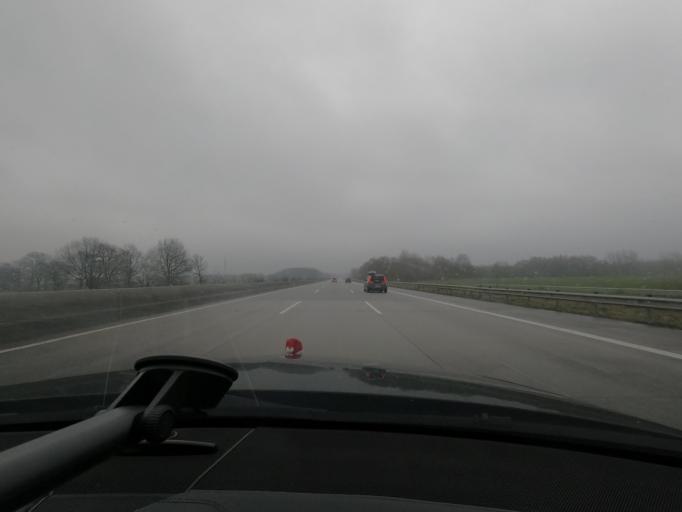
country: DE
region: Schleswig-Holstein
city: Schmalfeld
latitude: 53.8921
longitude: 9.9412
